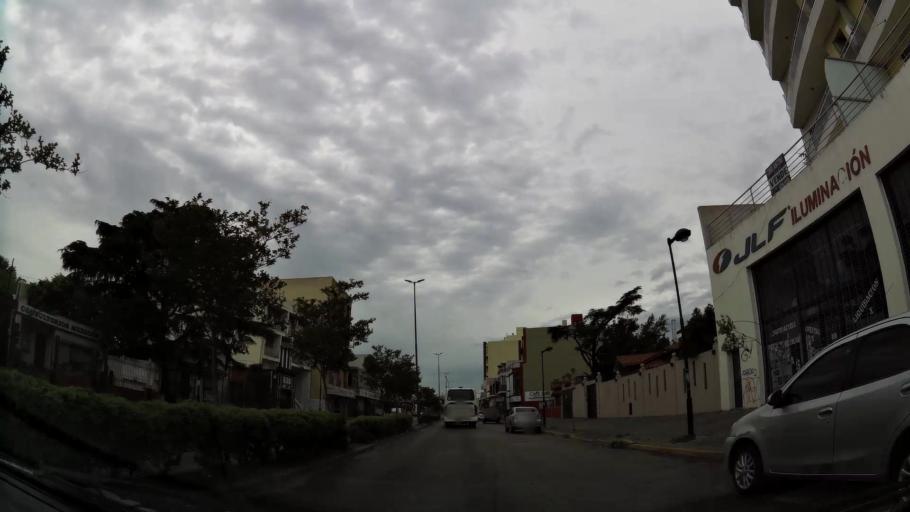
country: AR
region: Buenos Aires
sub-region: Partido de Quilmes
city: Quilmes
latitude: -34.7562
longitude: -58.2087
